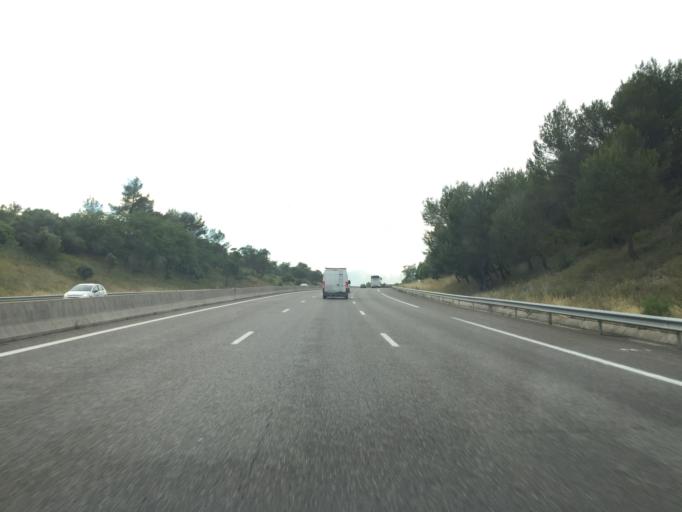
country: FR
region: Provence-Alpes-Cote d'Azur
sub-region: Departement du Var
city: Tourves
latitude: 43.4258
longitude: 5.9505
